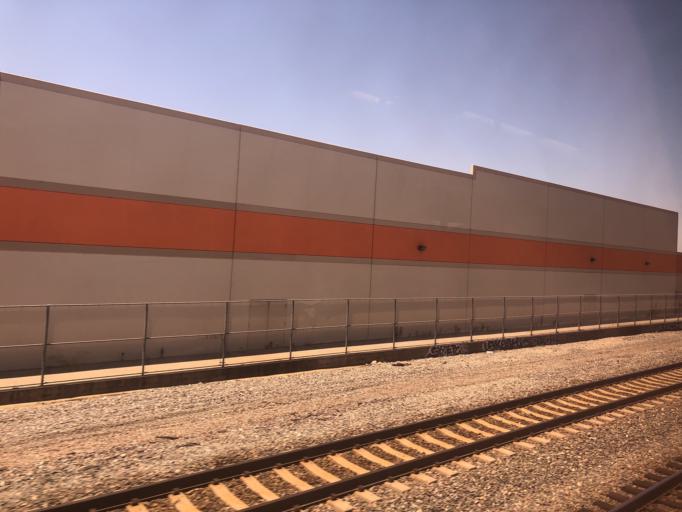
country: US
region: California
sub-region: Los Angeles County
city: Bell Gardens
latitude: 33.9874
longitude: -118.1338
